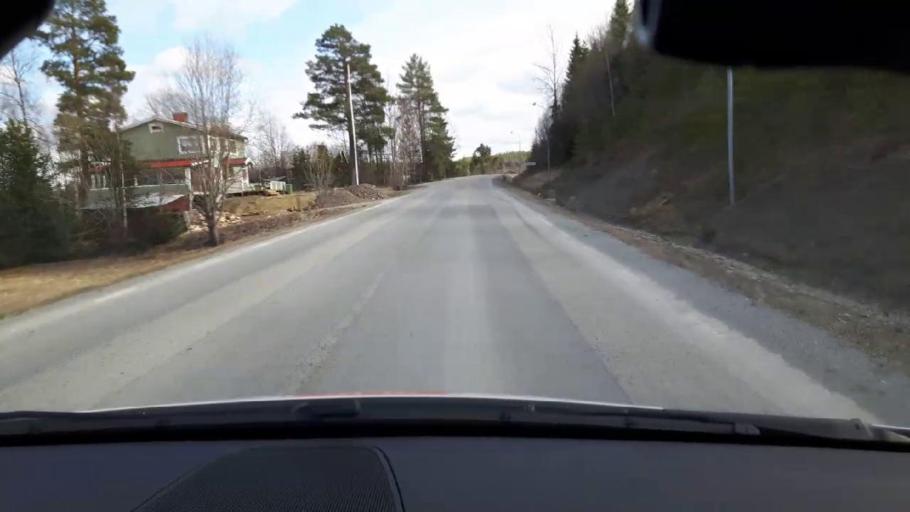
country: SE
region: Jaemtland
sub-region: Bergs Kommun
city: Hoverberg
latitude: 62.7811
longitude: 14.5117
